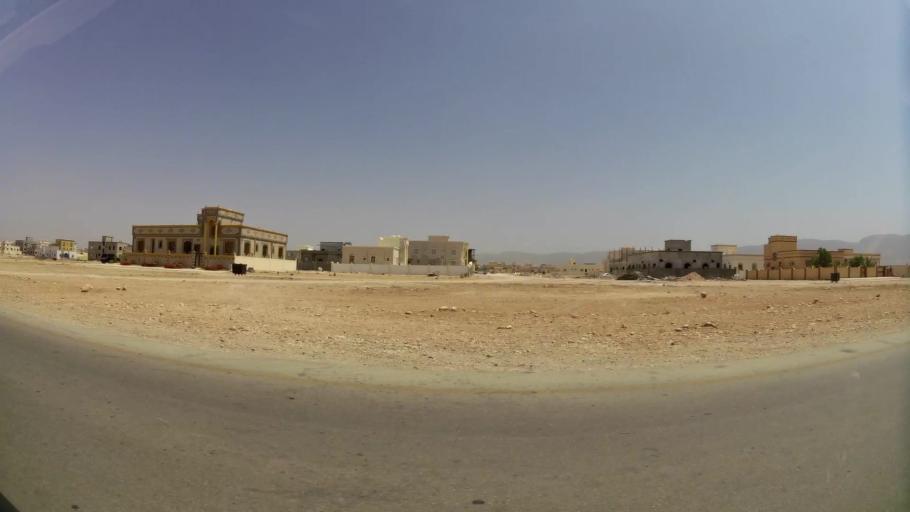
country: OM
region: Zufar
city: Salalah
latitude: 17.0686
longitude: 54.2152
